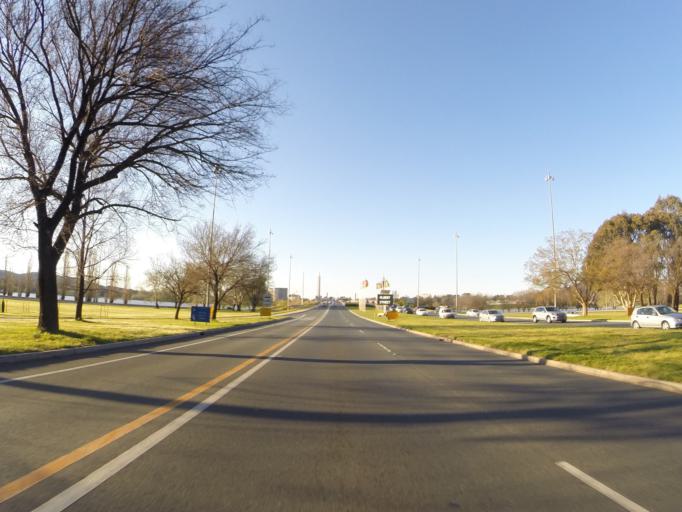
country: AU
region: Australian Capital Territory
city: Canberra
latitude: -35.2970
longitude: 149.1261
